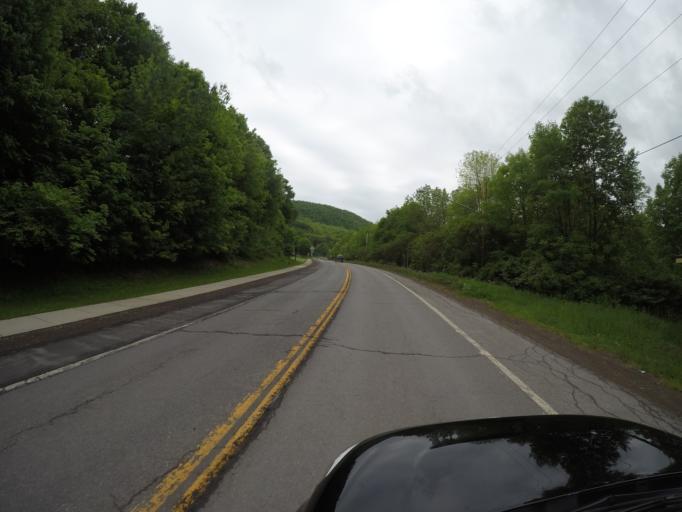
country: US
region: New York
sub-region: Delaware County
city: Delhi
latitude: 42.2722
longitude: -74.9166
